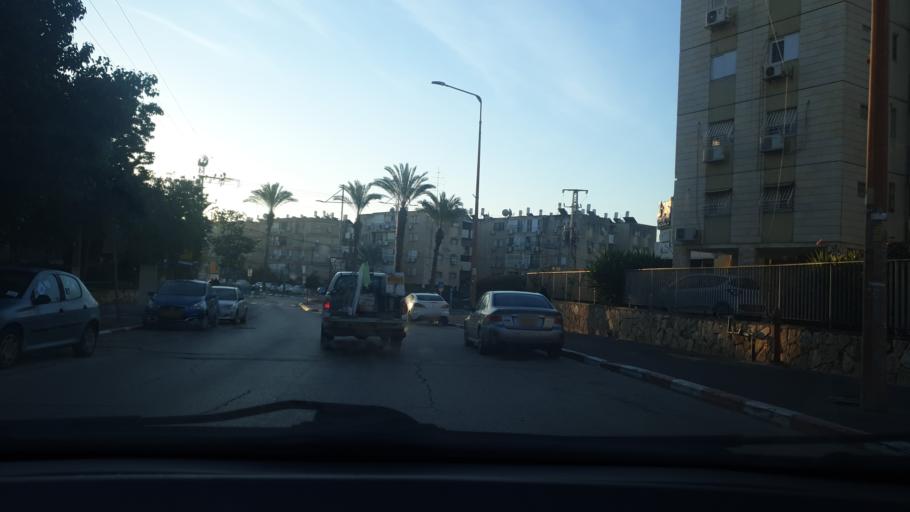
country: IL
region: Central District
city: Ramla
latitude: 31.9350
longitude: 34.8583
